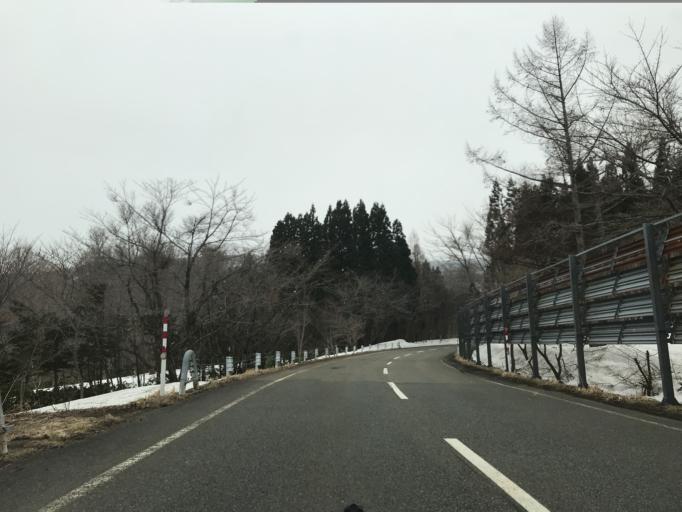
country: JP
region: Iwate
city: Ichinoseki
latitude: 39.0088
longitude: 140.8659
